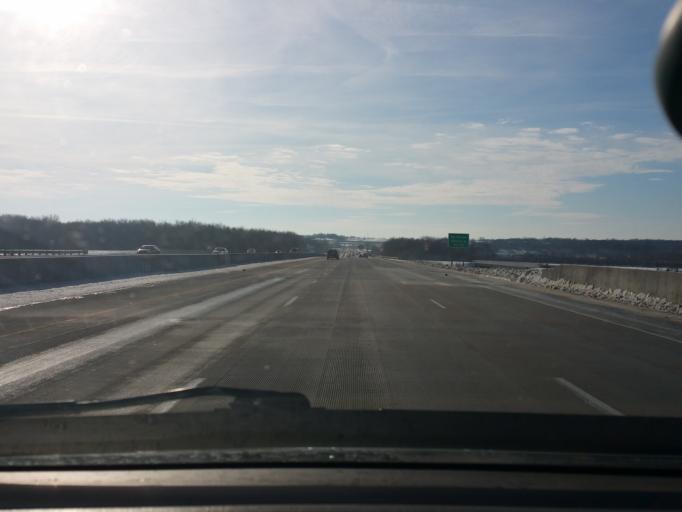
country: US
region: Iowa
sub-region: Polk County
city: West Des Moines
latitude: 41.5413
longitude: -93.7754
